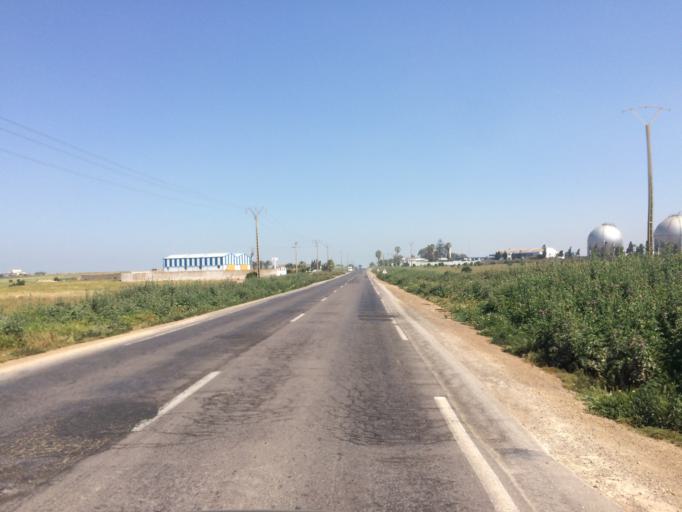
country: MA
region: Doukkala-Abda
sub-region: El-Jadida
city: Moulay Abdallah
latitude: 33.1626
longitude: -8.6030
